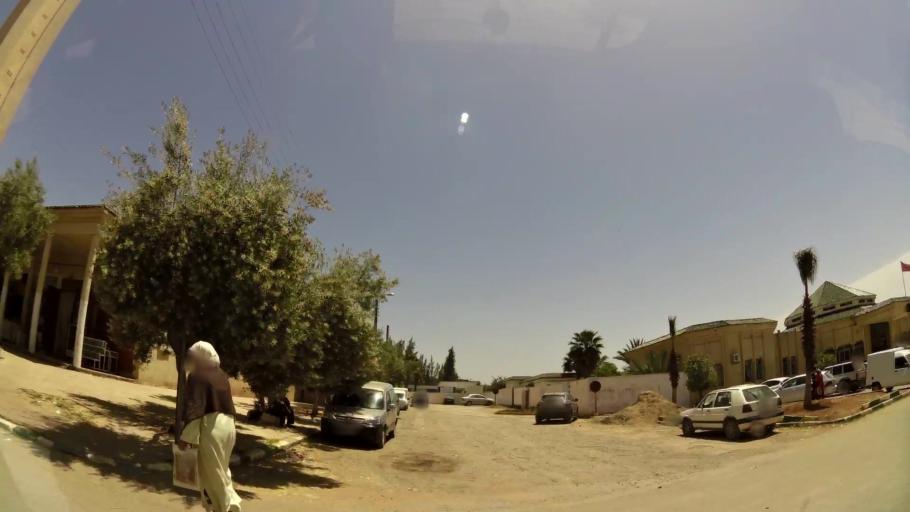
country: MA
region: Rabat-Sale-Zemmour-Zaer
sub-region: Khemisset
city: Khemisset
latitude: 33.8297
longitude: -6.0888
